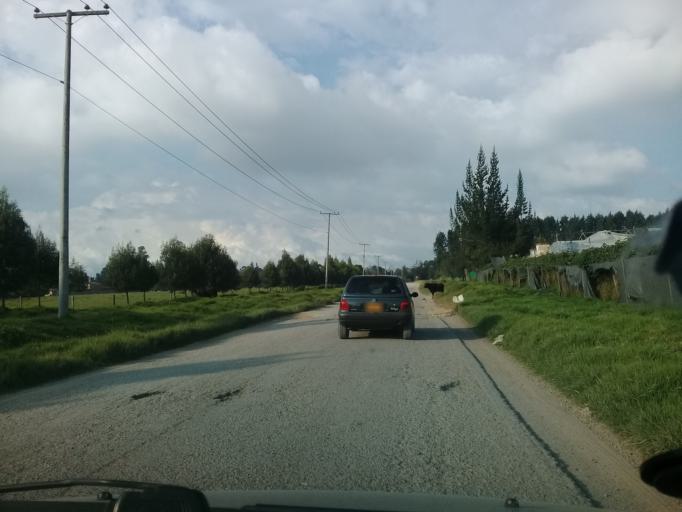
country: CO
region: Cundinamarca
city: Funza
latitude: 4.7568
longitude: -74.2238
